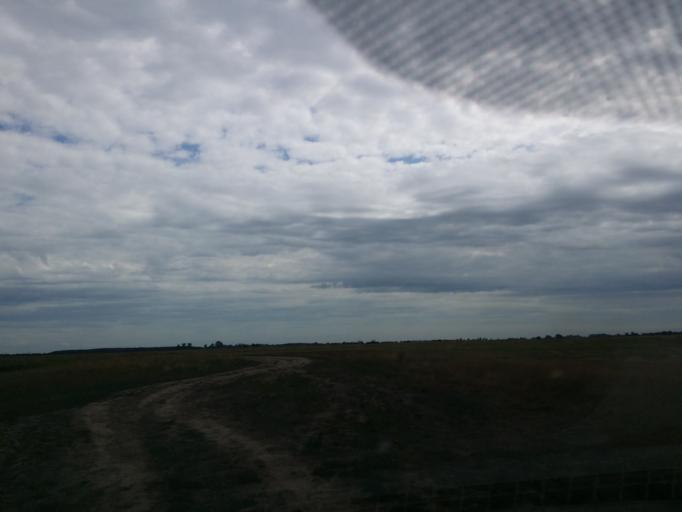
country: HU
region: Hajdu-Bihar
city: Egyek
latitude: 47.5544
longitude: 20.9428
